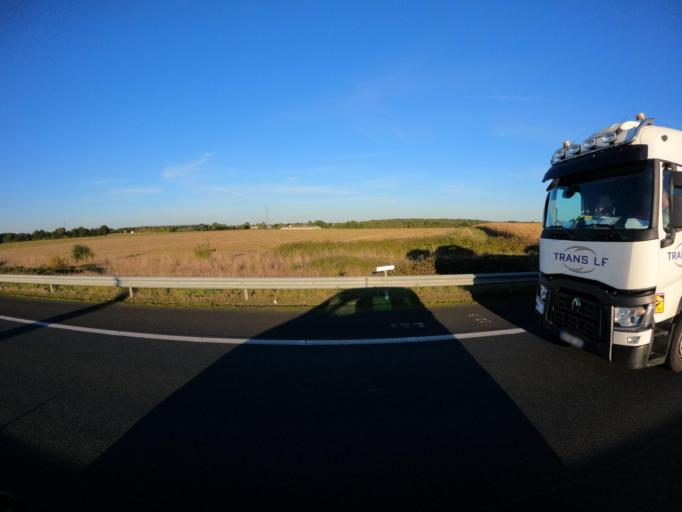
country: FR
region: Pays de la Loire
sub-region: Departement de la Vendee
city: Les Brouzils
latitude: 46.8873
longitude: -1.2935
